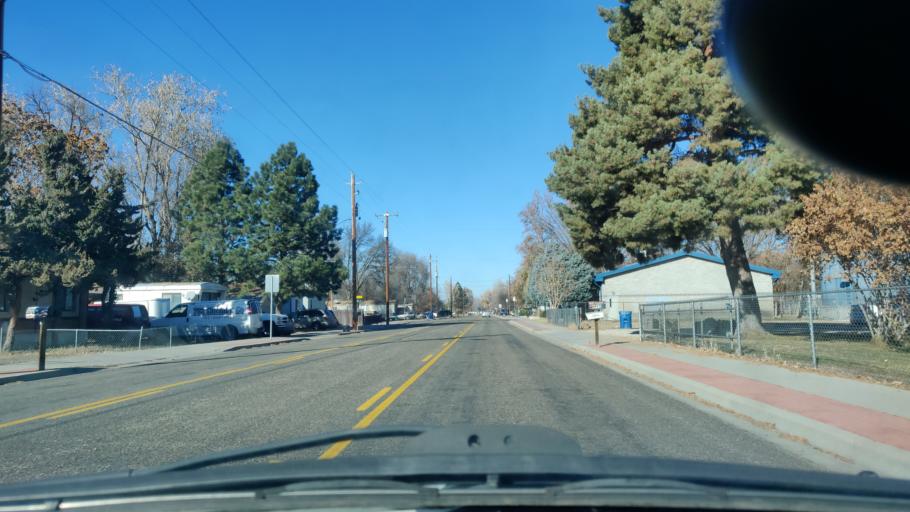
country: US
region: Idaho
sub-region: Ada County
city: Garden City
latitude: 43.6414
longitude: -116.2568
